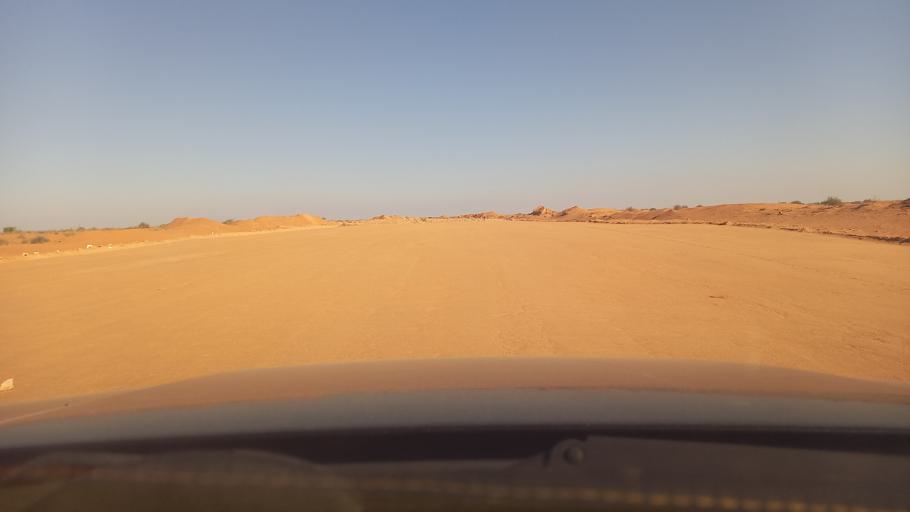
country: TN
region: Madanin
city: Medenine
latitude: 33.1599
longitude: 10.5179
